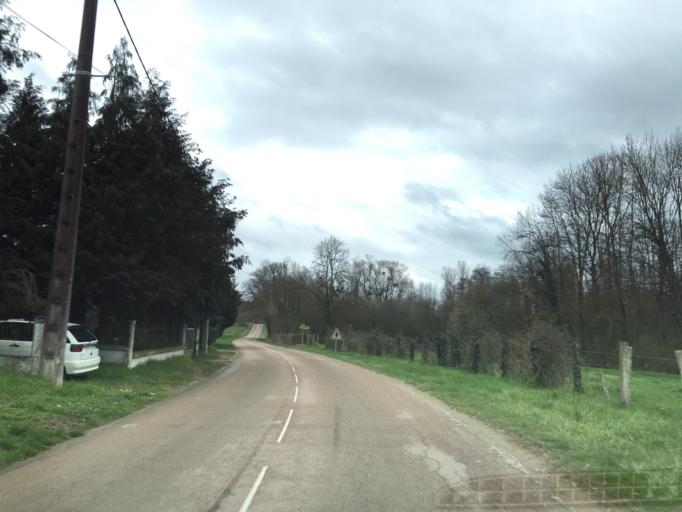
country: FR
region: Bourgogne
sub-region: Departement de l'Yonne
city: Pourrain
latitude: 47.8061
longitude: 3.3704
